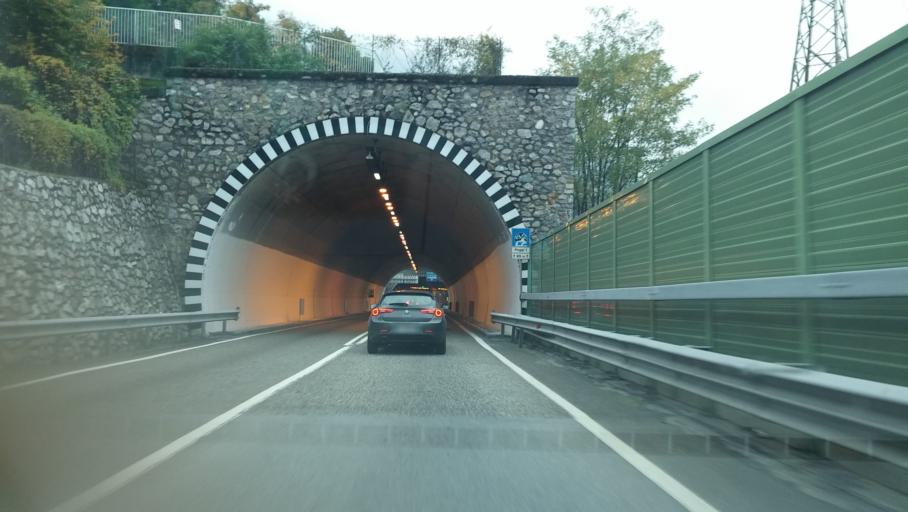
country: IT
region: Lombardy
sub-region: Provincia di Lecco
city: Lecco
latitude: 45.8605
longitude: 9.4156
